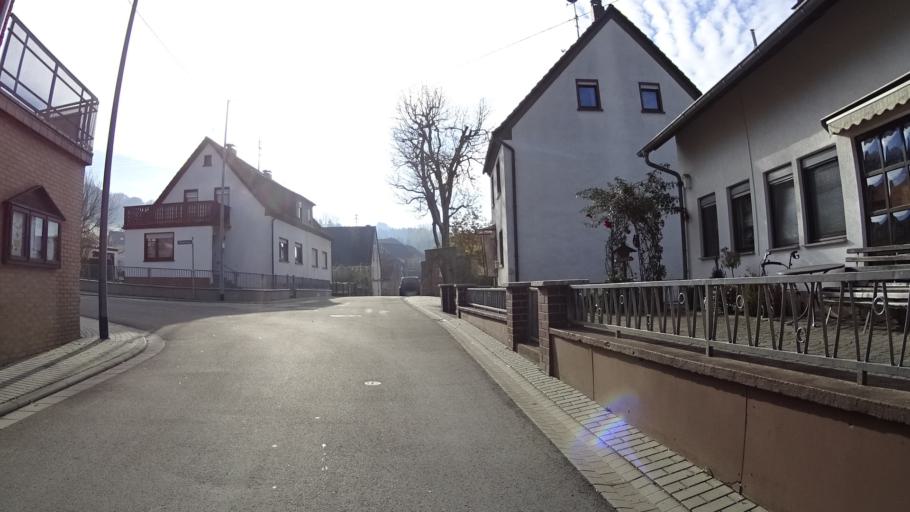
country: DE
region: Rheinland-Pfalz
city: Wiesweiler
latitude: 49.6372
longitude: 7.5726
